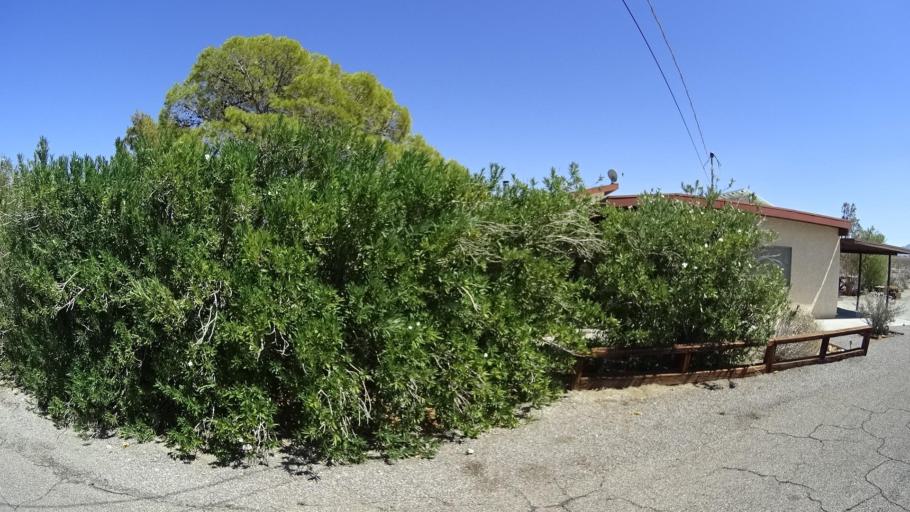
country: US
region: California
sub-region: San Diego County
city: Borrego Springs
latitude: 33.2065
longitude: -116.3456
